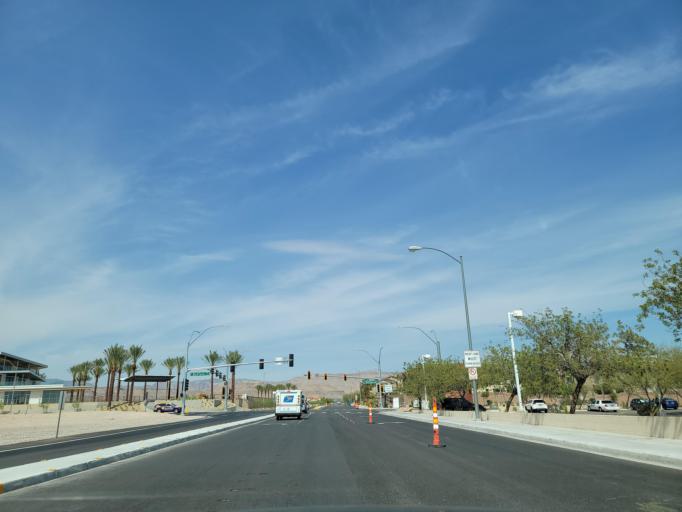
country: US
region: Nevada
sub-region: Clark County
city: Spring Valley
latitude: 36.0776
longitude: -115.2597
